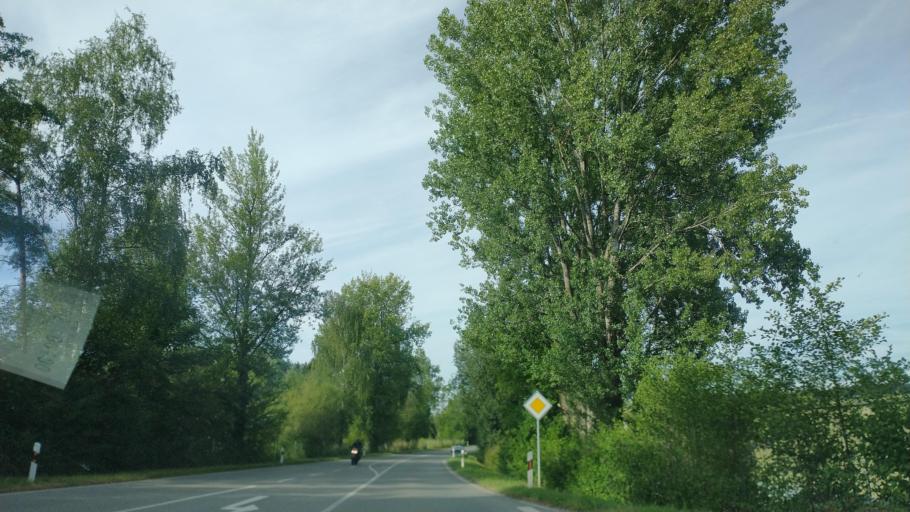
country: DE
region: Baden-Wuerttemberg
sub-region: Tuebingen Region
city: Kressbronn am Bodensee
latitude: 47.5999
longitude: 9.5797
